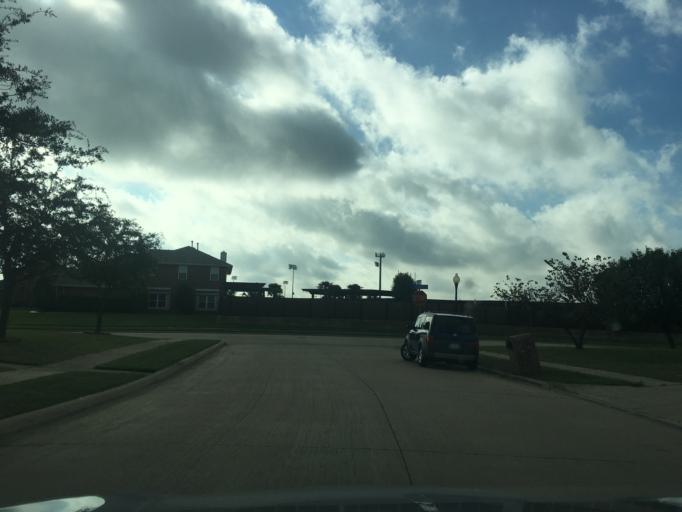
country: US
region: Texas
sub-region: Dallas County
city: Sachse
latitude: 32.9638
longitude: -96.5905
